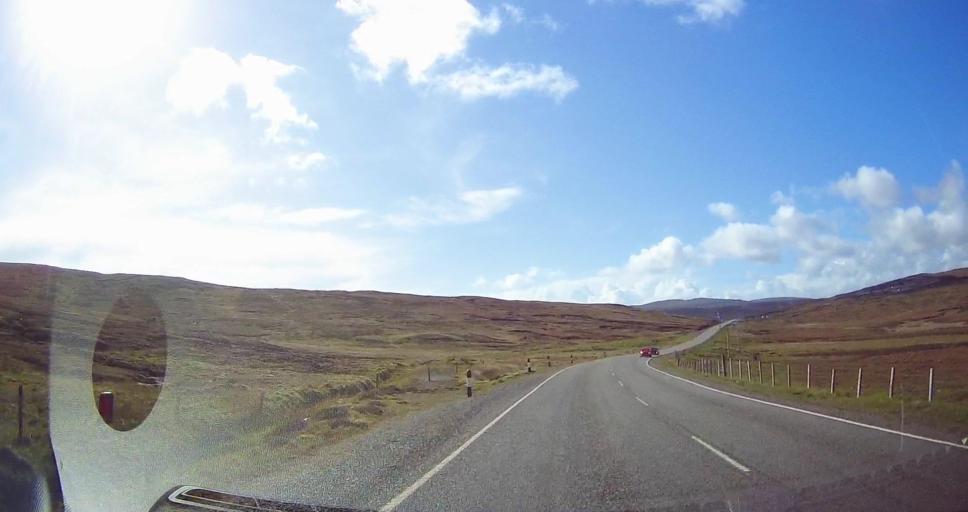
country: GB
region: Scotland
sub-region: Shetland Islands
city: Lerwick
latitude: 60.2678
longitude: -1.2294
